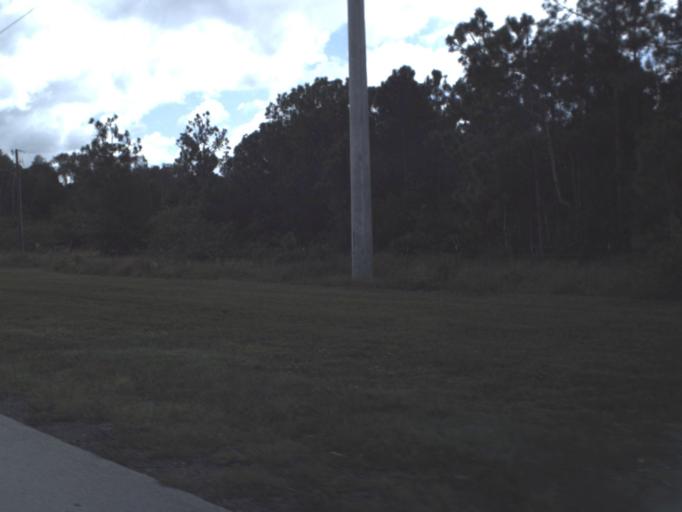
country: US
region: Florida
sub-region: Lee County
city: Gateway
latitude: 26.5797
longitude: -81.7090
